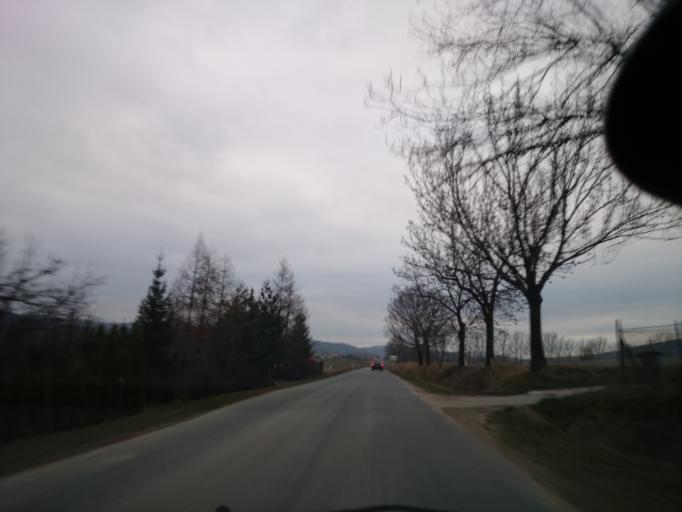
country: PL
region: Lower Silesian Voivodeship
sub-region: Powiat zabkowicki
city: Bardo
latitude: 50.5316
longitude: 16.7453
